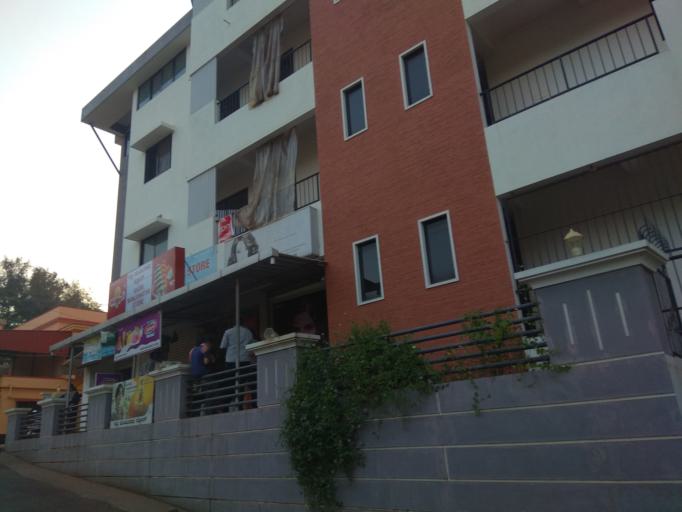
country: IN
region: Karnataka
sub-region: Dakshina Kannada
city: Mangalore
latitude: 12.8938
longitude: 74.8532
